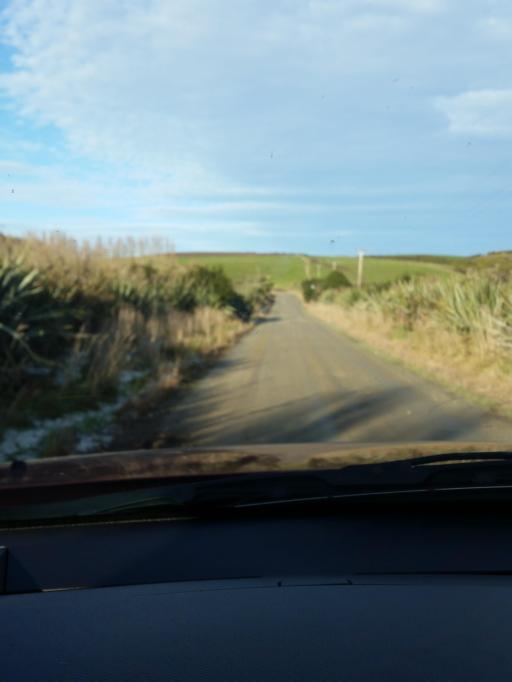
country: NZ
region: Southland
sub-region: Gore District
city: Gore
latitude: -46.2052
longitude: 168.7674
